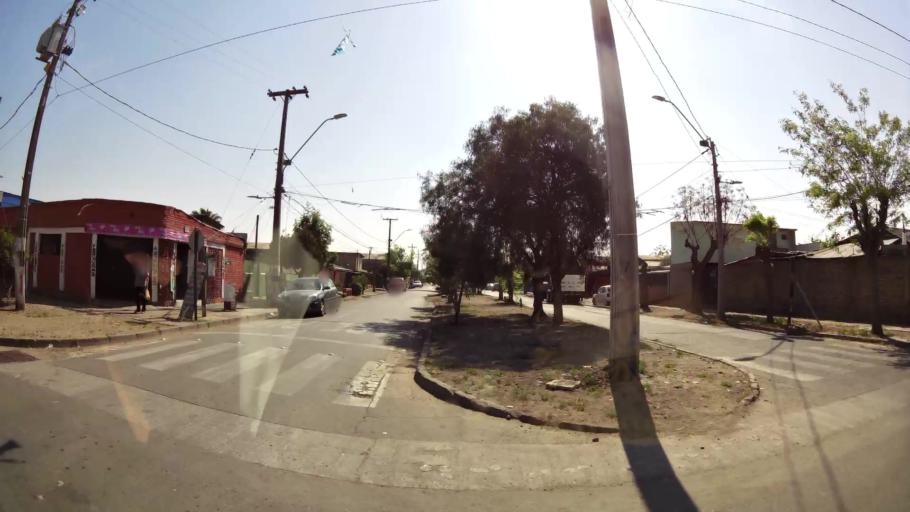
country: CL
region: Santiago Metropolitan
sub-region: Provincia de Maipo
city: San Bernardo
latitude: -33.5882
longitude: -70.6906
